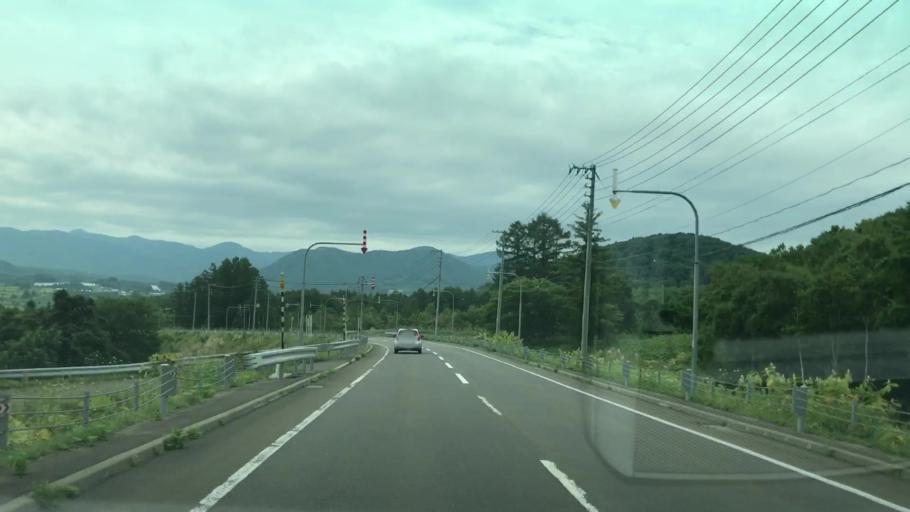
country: JP
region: Hokkaido
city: Yoichi
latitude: 43.1119
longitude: 140.8194
